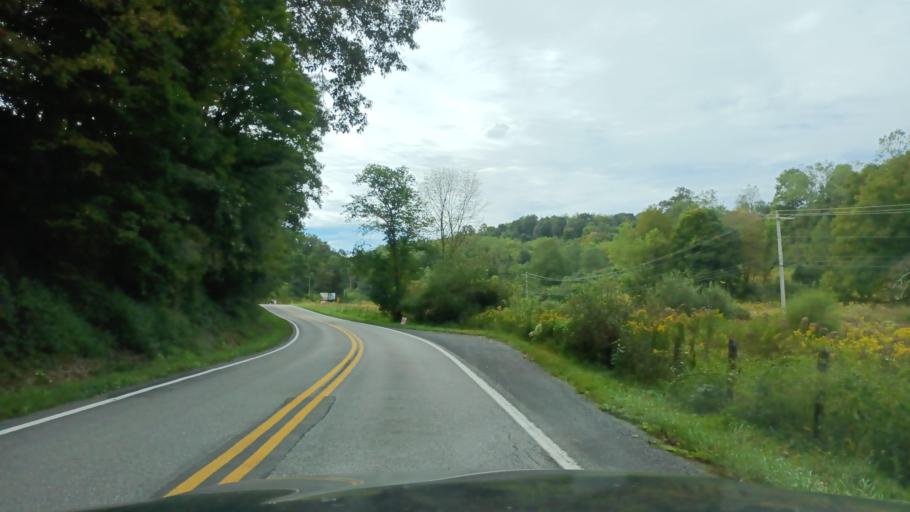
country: US
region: West Virginia
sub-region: Taylor County
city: Grafton
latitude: 39.3273
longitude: -80.1127
